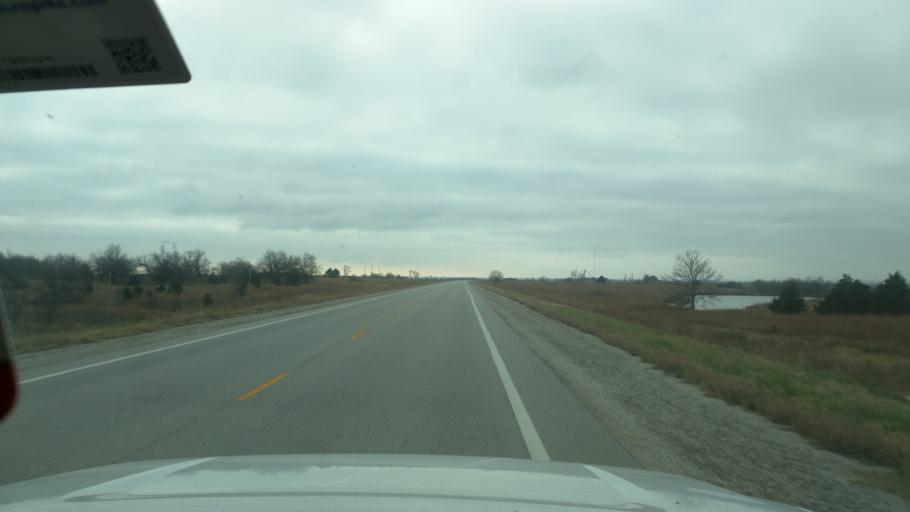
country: US
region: Kansas
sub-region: Elk County
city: Howard
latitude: 37.5673
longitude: -96.2532
